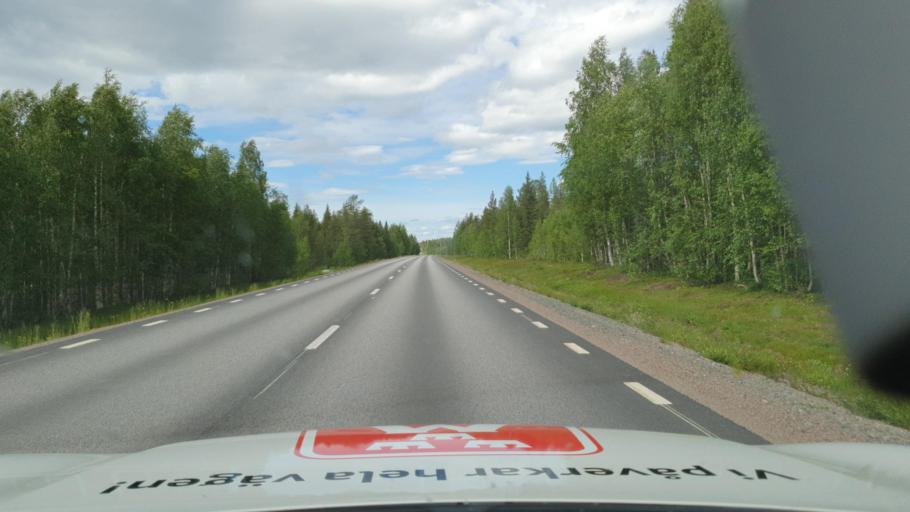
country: SE
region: Vaesterbotten
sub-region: Norsjo Kommun
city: Norsjoe
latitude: 65.1825
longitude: 19.8518
